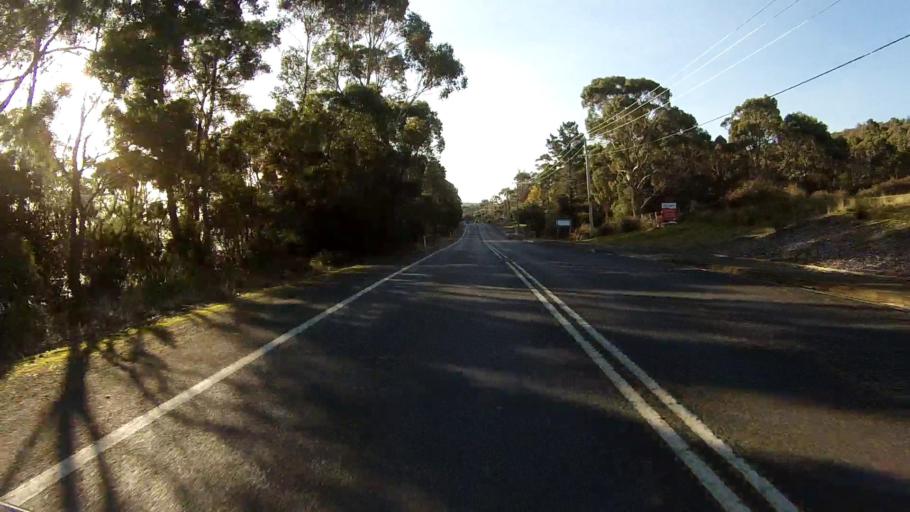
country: AU
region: Tasmania
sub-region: Clarence
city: Sandford
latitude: -43.0485
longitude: 147.8654
